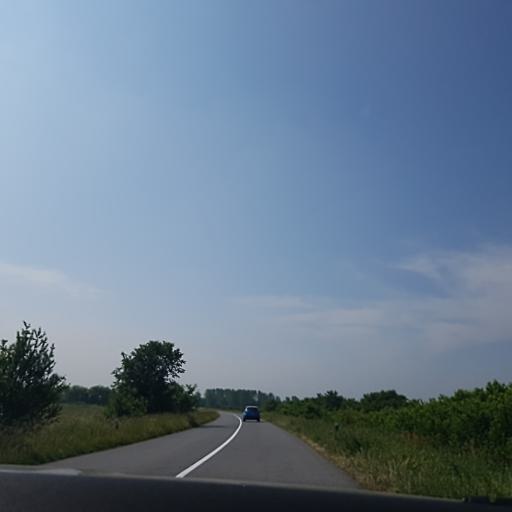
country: RS
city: Jarkovac
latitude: 45.2804
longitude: 20.7624
